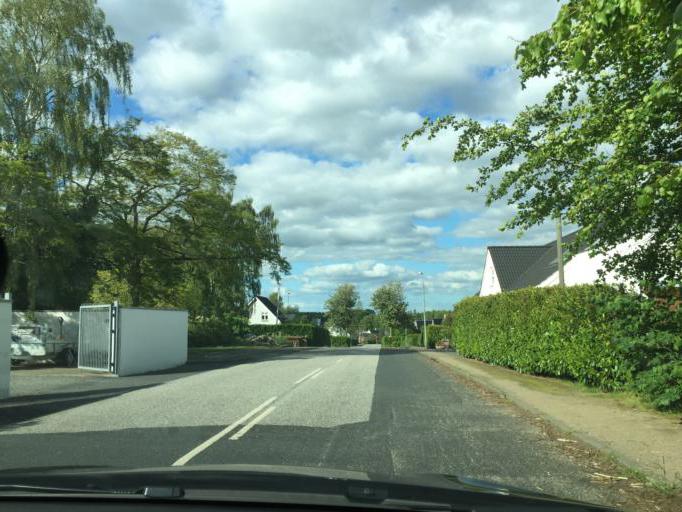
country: DK
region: South Denmark
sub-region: Odense Kommune
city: Bellinge
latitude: 55.3349
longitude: 10.3094
